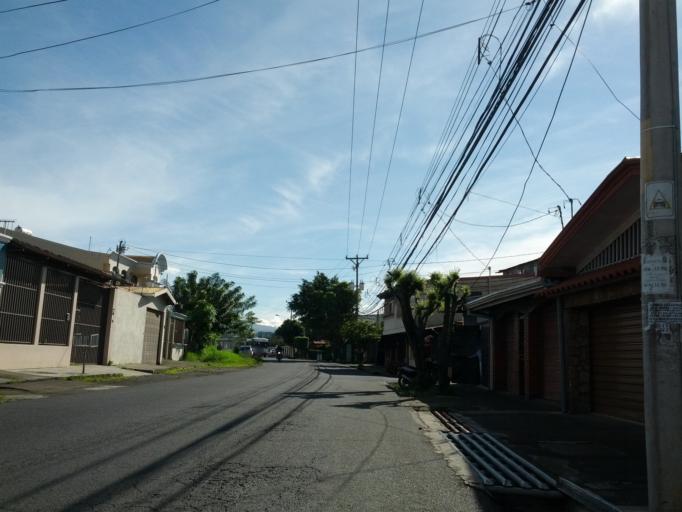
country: CR
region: Alajuela
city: Alajuela
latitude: 10.0179
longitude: -84.2035
